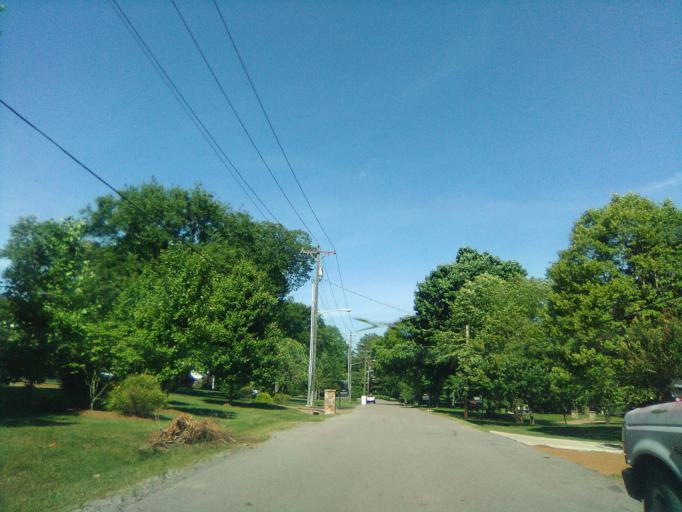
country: US
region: Tennessee
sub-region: Davidson County
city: Belle Meade
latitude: 36.1177
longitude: -86.8288
